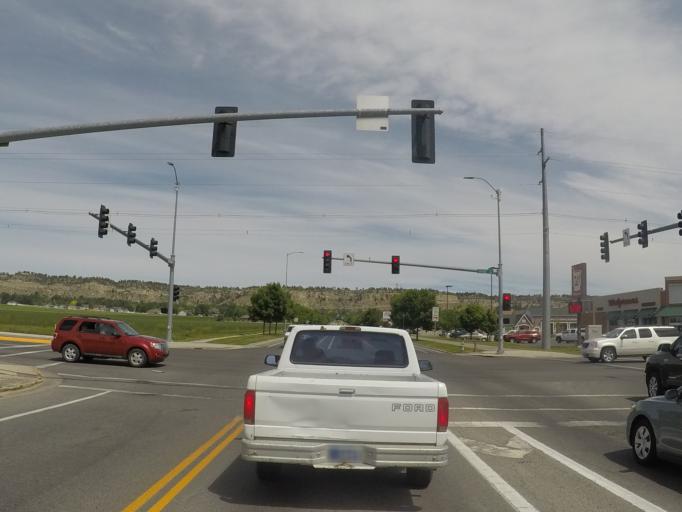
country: US
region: Montana
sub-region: Yellowstone County
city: Billings
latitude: 45.7838
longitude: -108.6007
